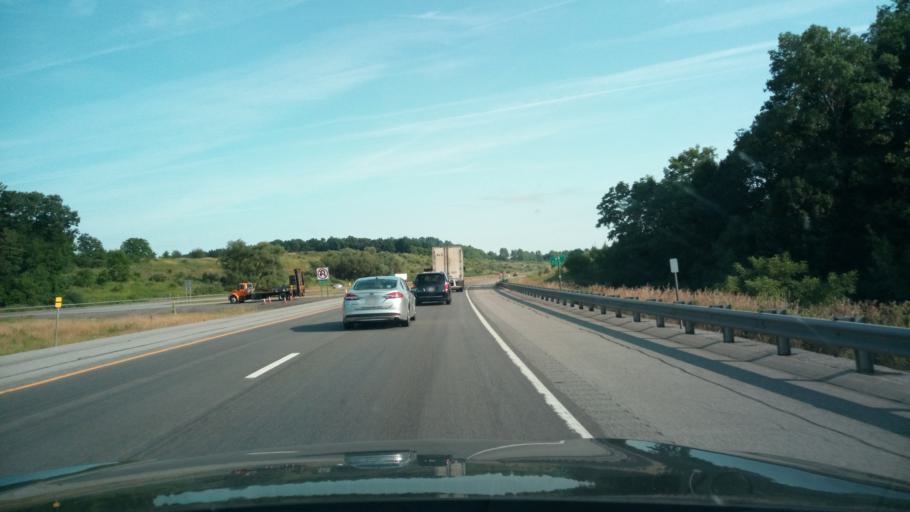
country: US
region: New York
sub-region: Livingston County
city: Mount Morris
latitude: 42.6637
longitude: -77.8114
